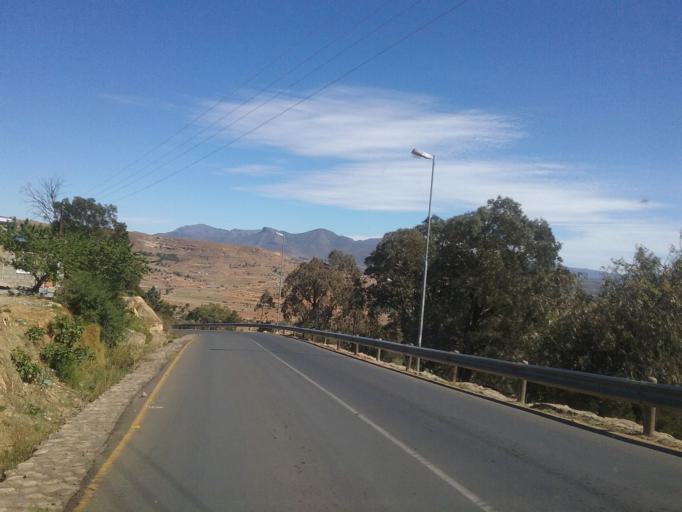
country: LS
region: Quthing
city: Quthing
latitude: -30.4034
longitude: 27.7089
